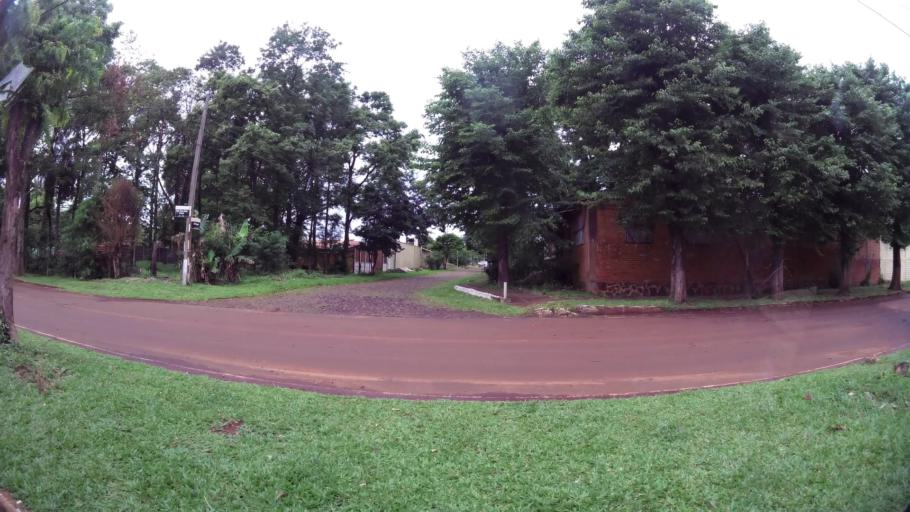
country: PY
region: Alto Parana
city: Presidente Franco
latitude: -25.4882
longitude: -54.7677
